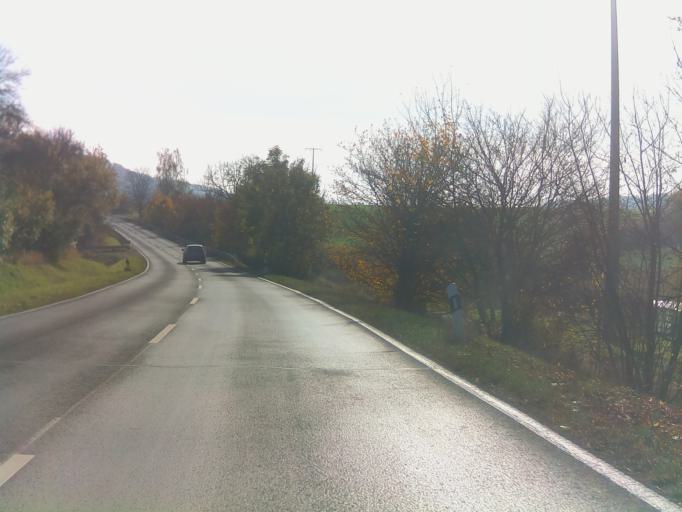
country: DE
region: Bavaria
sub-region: Regierungsbezirk Unterfranken
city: Knetzgau
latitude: 49.9118
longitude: 10.5553
